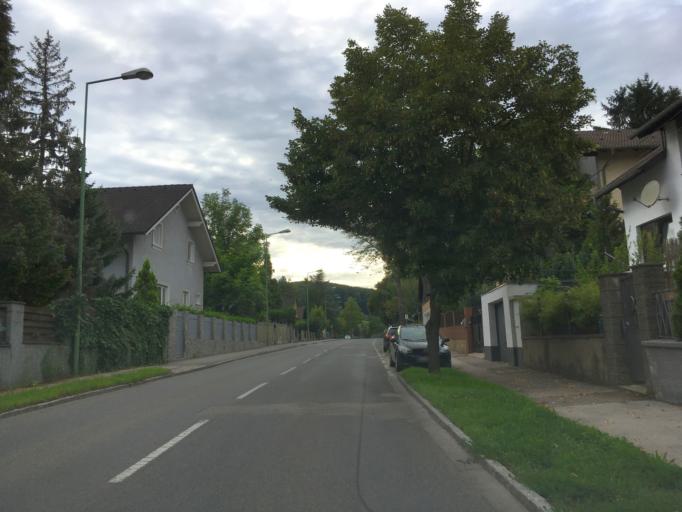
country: AT
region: Lower Austria
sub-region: Politischer Bezirk Tulln
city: Wordern
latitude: 48.3138
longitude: 16.2453
